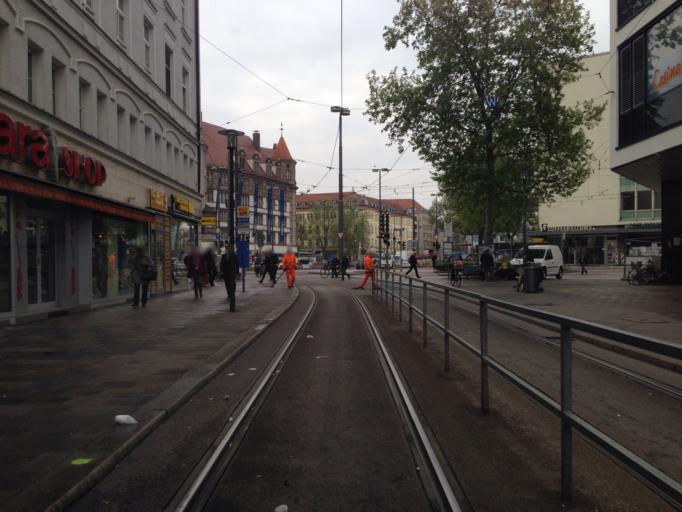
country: DE
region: Bavaria
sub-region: Upper Bavaria
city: Munich
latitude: 48.1416
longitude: 11.5606
